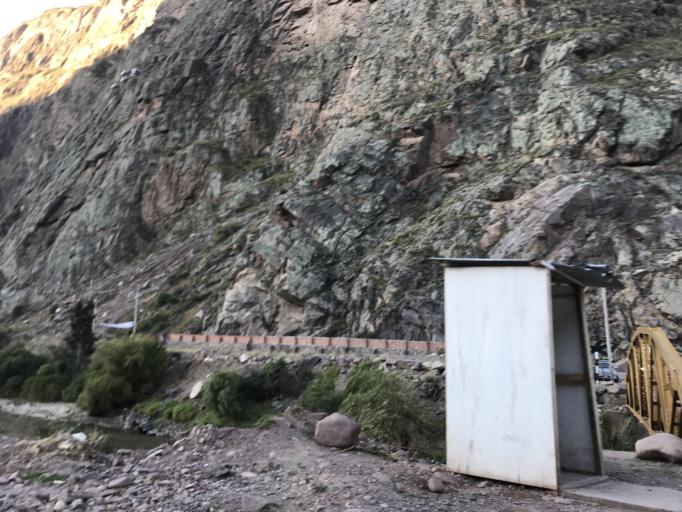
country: PE
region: Cusco
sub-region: Provincia de Urubamba
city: Ollantaytambo
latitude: -13.2745
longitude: -72.2171
